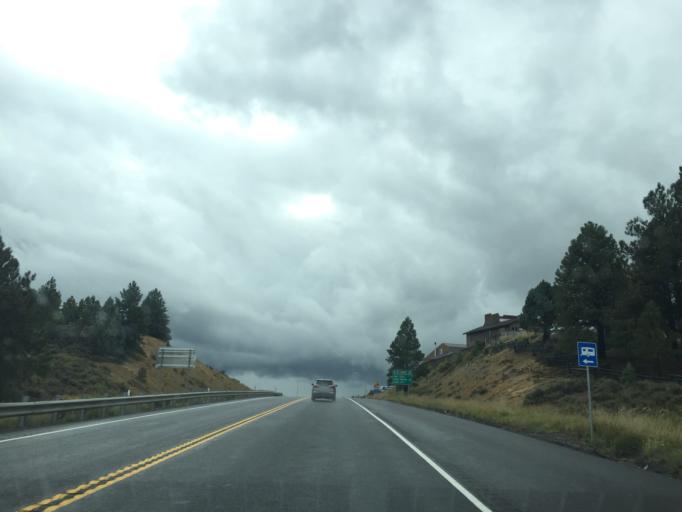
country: US
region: Utah
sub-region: Garfield County
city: Panguitch
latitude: 37.4909
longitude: -112.5113
